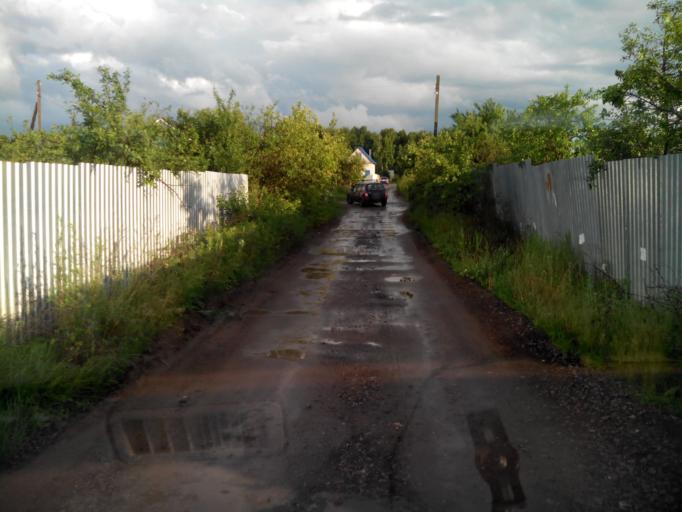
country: RU
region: Penza
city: Zasechnoye
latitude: 53.0387
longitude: 45.0483
